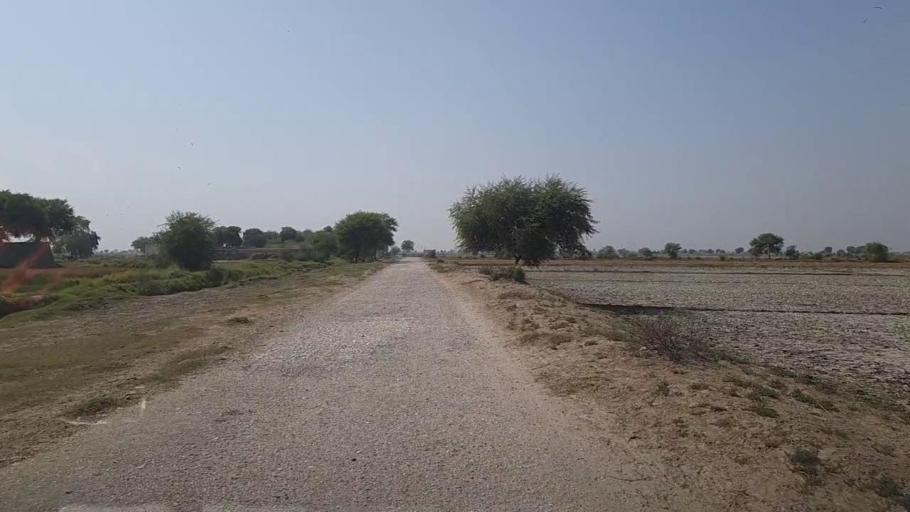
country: PK
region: Sindh
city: Kandhkot
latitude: 28.3876
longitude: 69.3211
